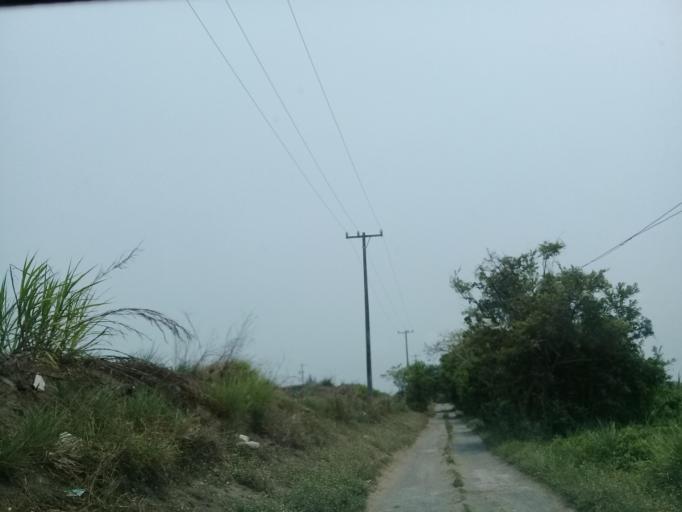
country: MX
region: Veracruz
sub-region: Veracruz
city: Hacienda Sotavento
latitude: 19.1432
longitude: -96.1592
